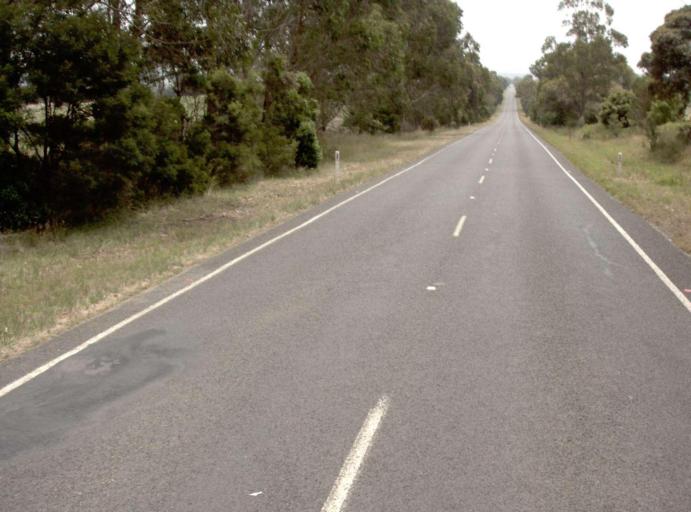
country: AU
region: Victoria
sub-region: Latrobe
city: Traralgon
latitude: -38.5053
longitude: 146.7101
